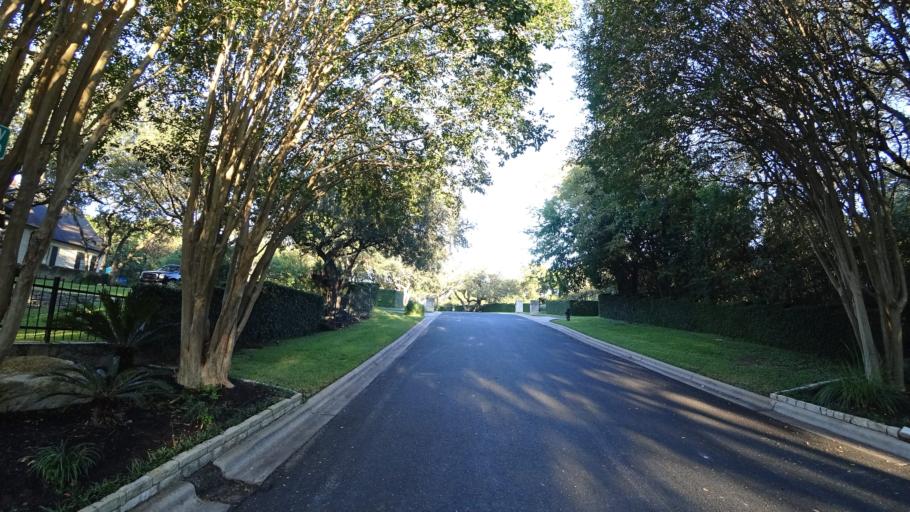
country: US
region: Texas
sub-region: Travis County
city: West Lake Hills
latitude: 30.3414
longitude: -97.8095
